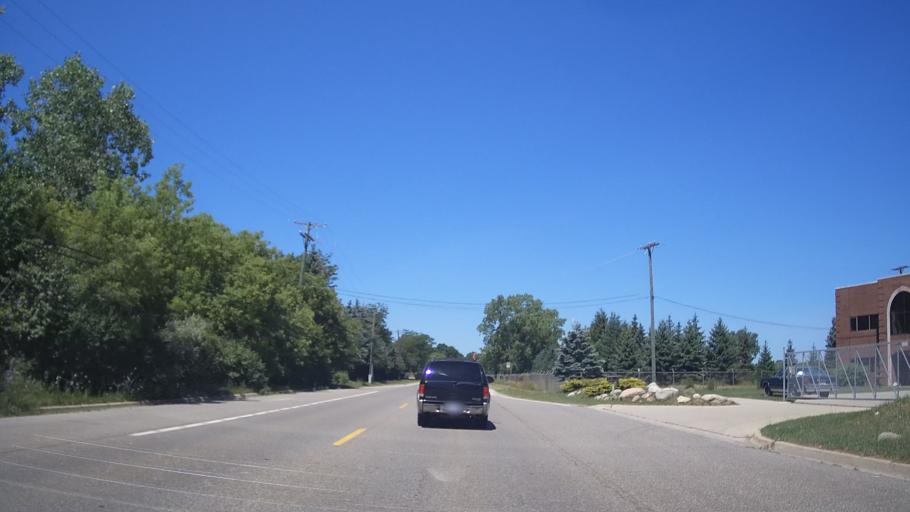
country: US
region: Michigan
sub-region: Macomb County
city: Shelby
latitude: 42.6529
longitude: -83.0850
